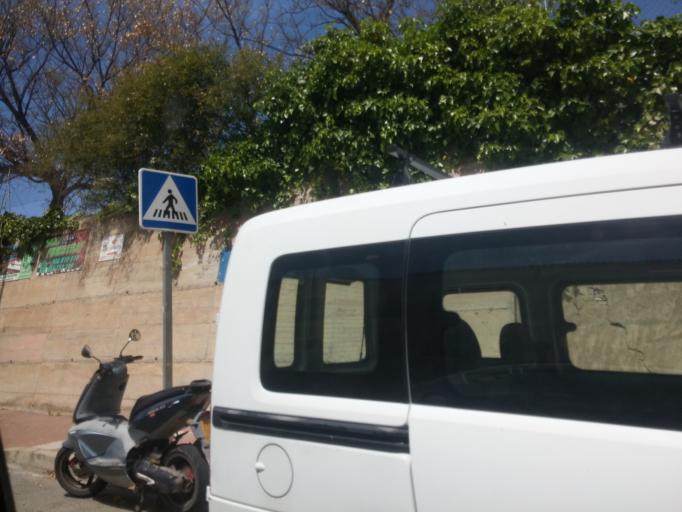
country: ES
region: Valencia
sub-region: Provincia de Alicante
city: Finestrat
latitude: 38.5691
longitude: -0.2135
